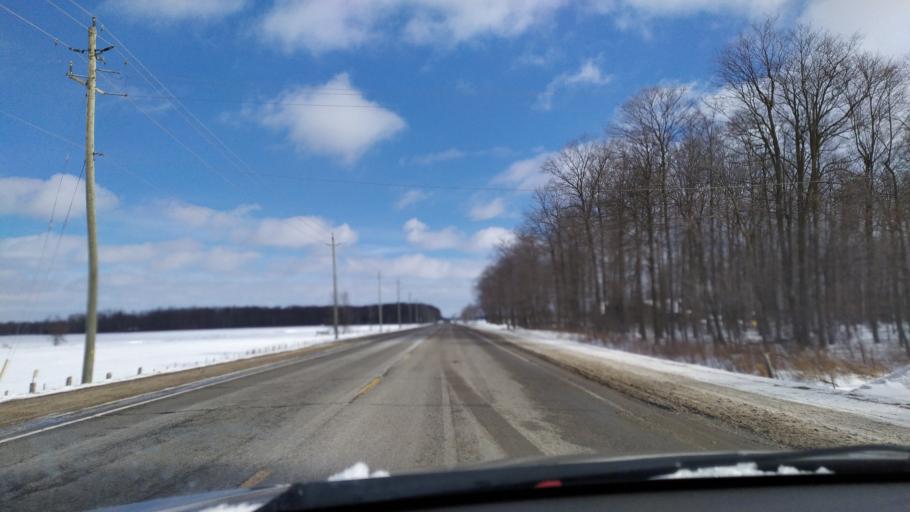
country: CA
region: Ontario
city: Waterloo
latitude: 43.5795
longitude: -80.5988
